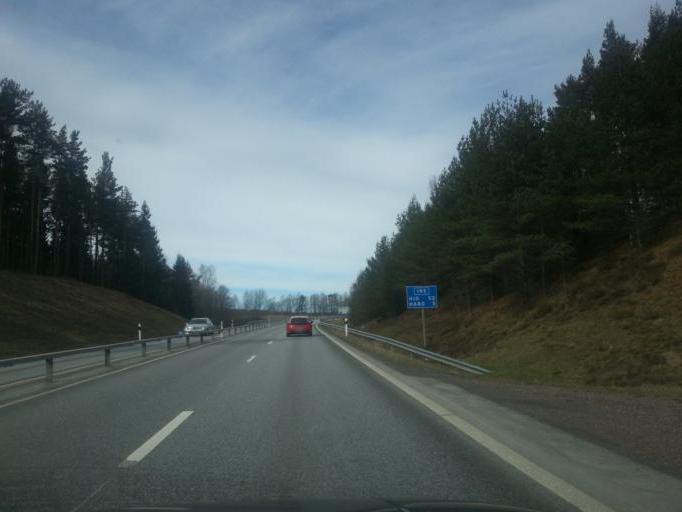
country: SE
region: Joenkoeping
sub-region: Jonkopings Kommun
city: Bankeryd
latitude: 57.8698
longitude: 14.1022
